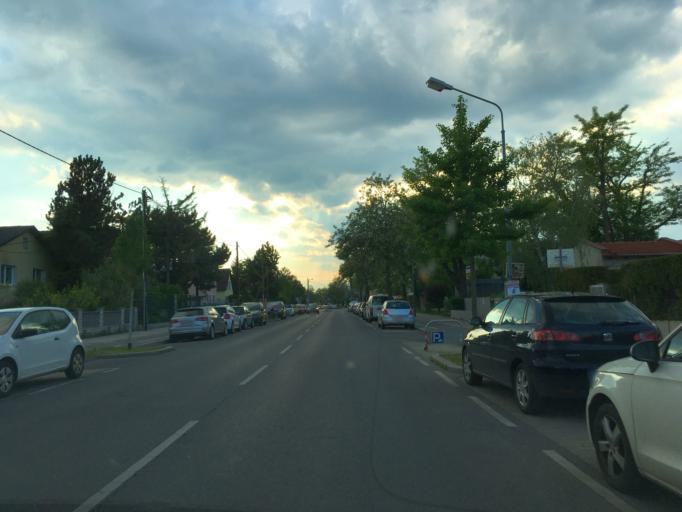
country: AT
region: Lower Austria
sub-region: Politischer Bezirk Wien-Umgebung
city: Gerasdorf bei Wien
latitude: 48.2858
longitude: 16.4366
